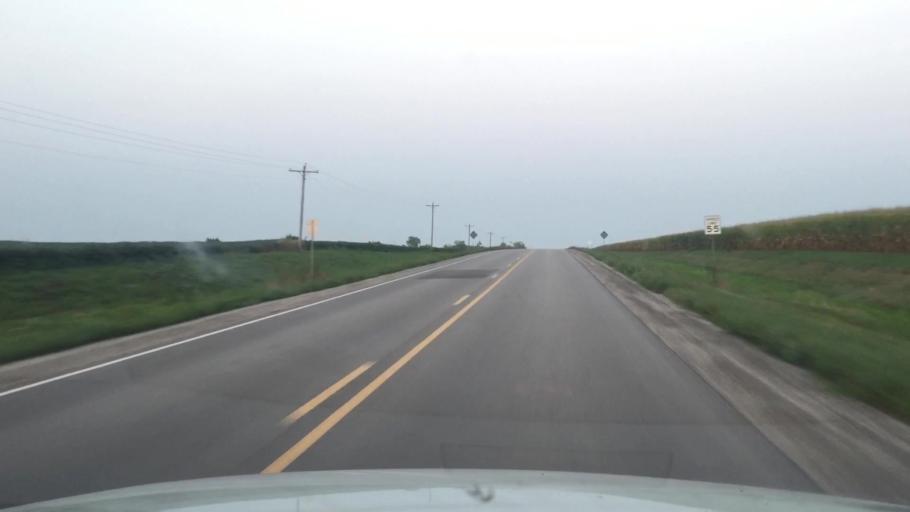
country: US
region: Iowa
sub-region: Warren County
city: Indianola
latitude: 41.1828
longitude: -93.4967
